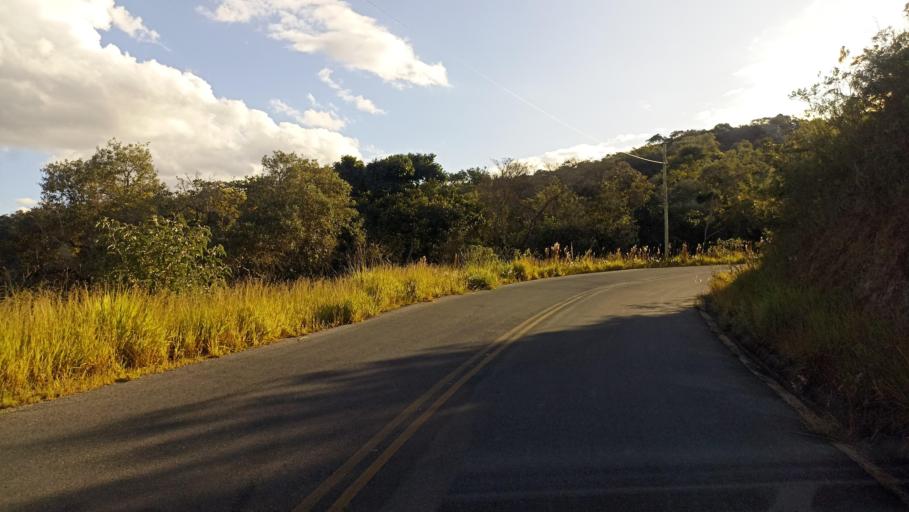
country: BR
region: Minas Gerais
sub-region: Ouro Preto
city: Ouro Preto
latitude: -20.3224
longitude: -43.6185
